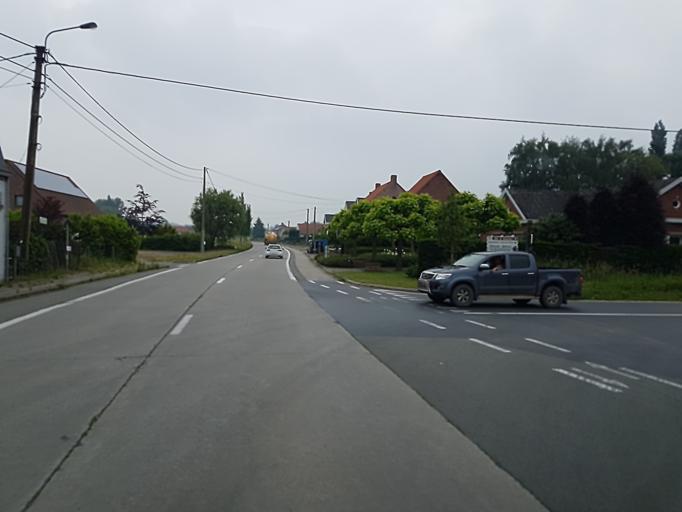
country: BE
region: Flanders
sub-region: Provincie West-Vlaanderen
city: Anzegem
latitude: 50.8518
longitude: 3.4630
